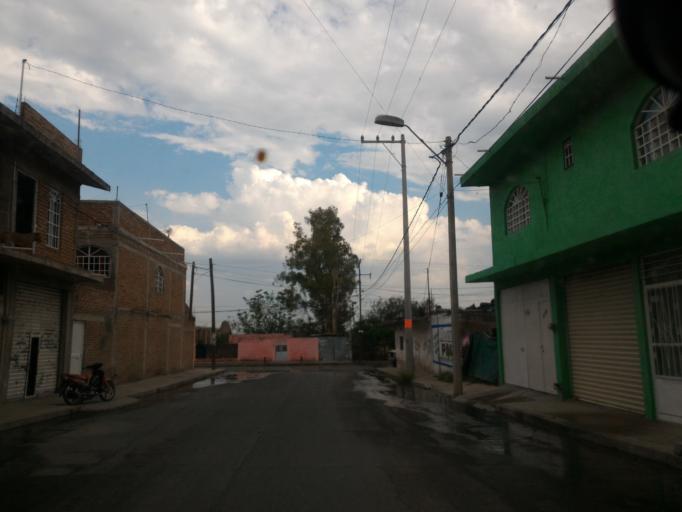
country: MX
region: Guanajuato
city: San Francisco del Rincon
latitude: 21.0393
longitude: -101.8561
